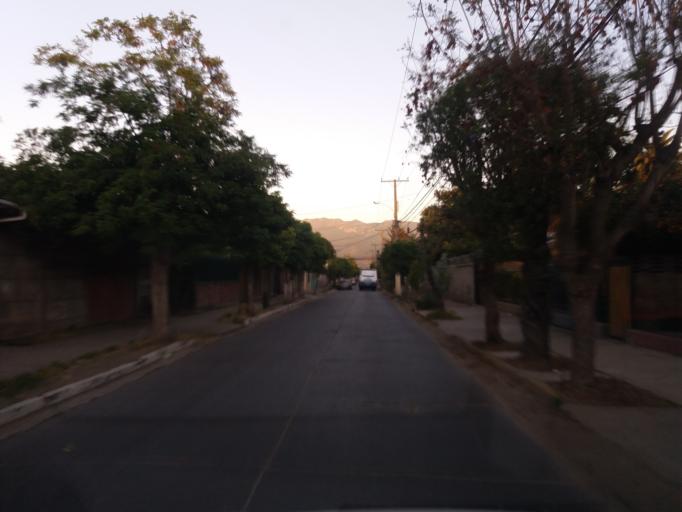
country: CL
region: Valparaiso
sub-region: Provincia de Quillota
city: Quillota
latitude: -32.8814
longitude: -71.2533
